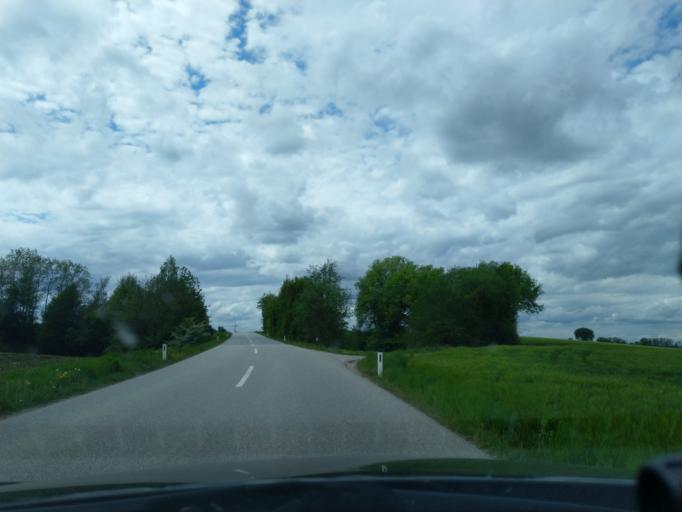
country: AT
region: Upper Austria
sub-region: Politischer Bezirk Scharding
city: Sankt Marienkirchen bei Schaerding
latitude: 48.3427
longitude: 13.3920
